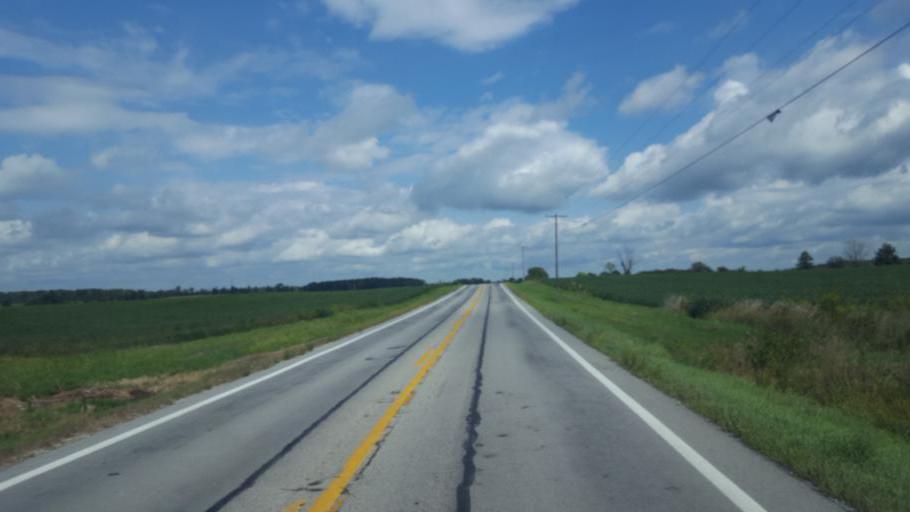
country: US
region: Ohio
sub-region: Seneca County
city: Tiffin
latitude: 41.0900
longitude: -83.0152
